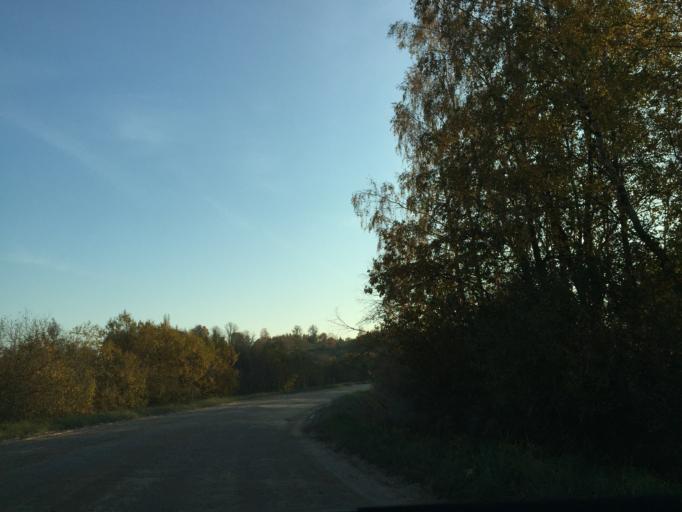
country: LV
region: Vainode
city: Vainode
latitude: 56.5272
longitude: 21.8278
